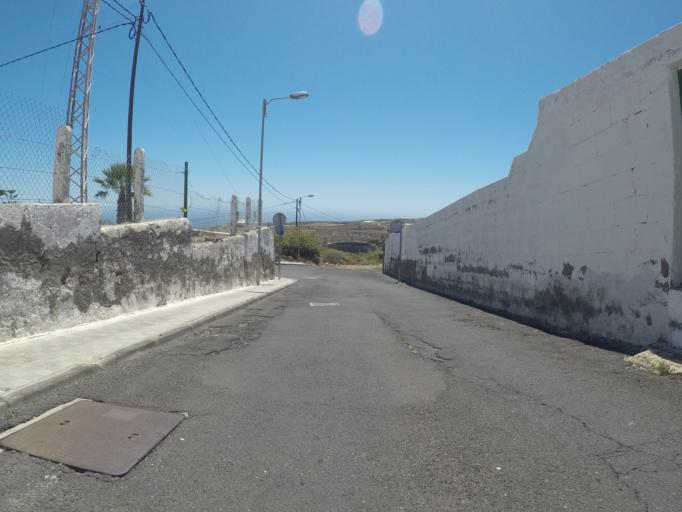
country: ES
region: Canary Islands
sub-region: Provincia de Santa Cruz de Tenerife
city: Lomo de Arico
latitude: 28.1808
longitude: -16.4837
